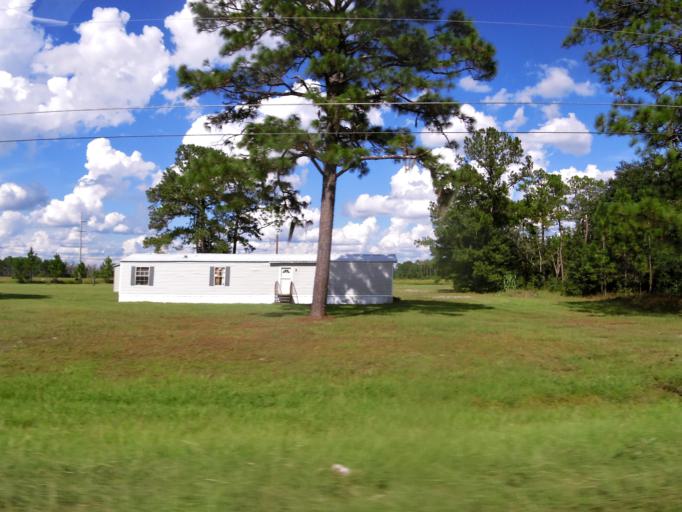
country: US
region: Georgia
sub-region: Lowndes County
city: Valdosta
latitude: 30.7842
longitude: -83.1655
